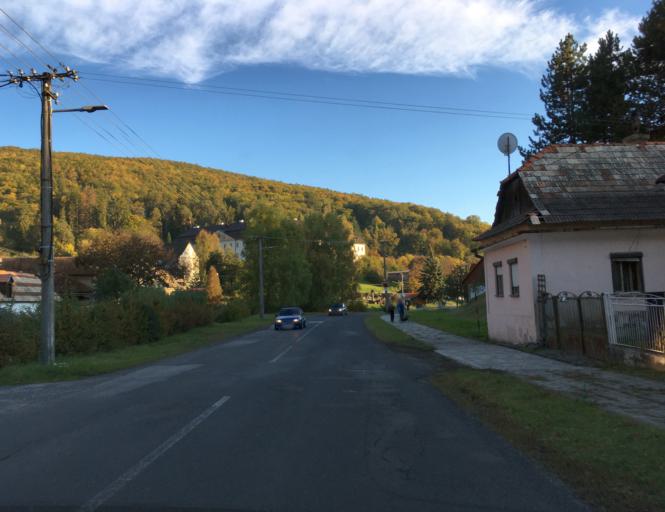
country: SK
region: Banskobystricky
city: Svaety Anton
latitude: 48.4235
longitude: 18.9404
